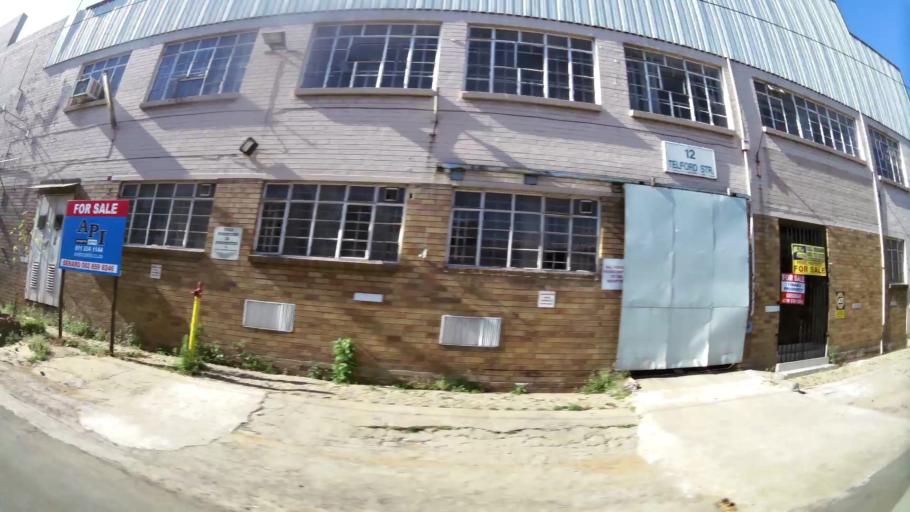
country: ZA
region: Gauteng
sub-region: City of Johannesburg Metropolitan Municipality
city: Johannesburg
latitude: -26.2006
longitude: 27.9790
